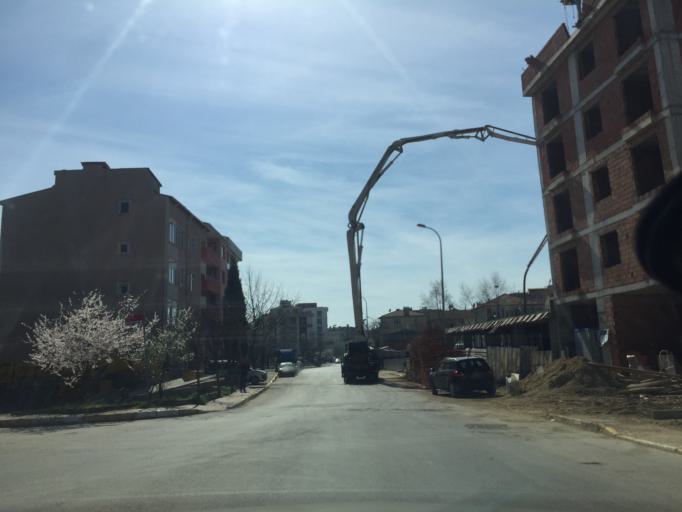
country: TR
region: Istanbul
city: Icmeler
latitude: 40.8301
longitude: 29.3193
